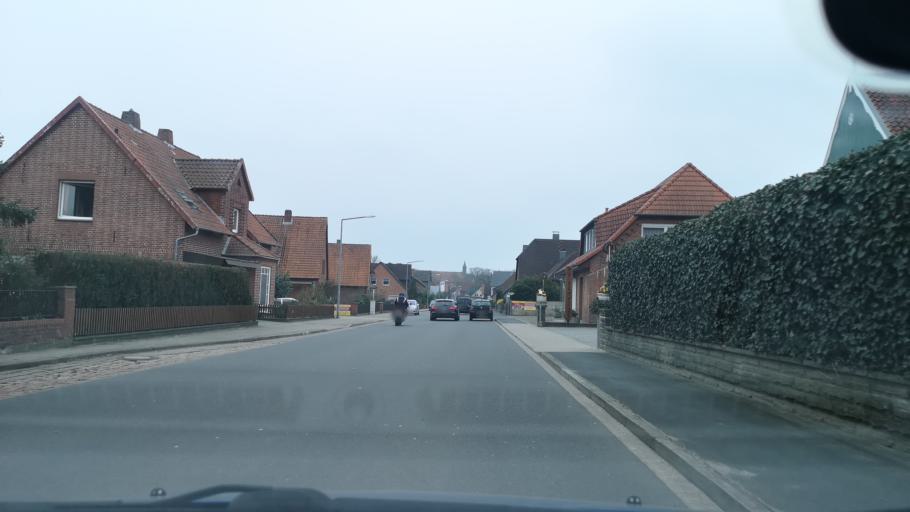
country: DE
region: Lower Saxony
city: Neustadt am Rubenberge
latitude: 52.5638
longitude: 9.4871
